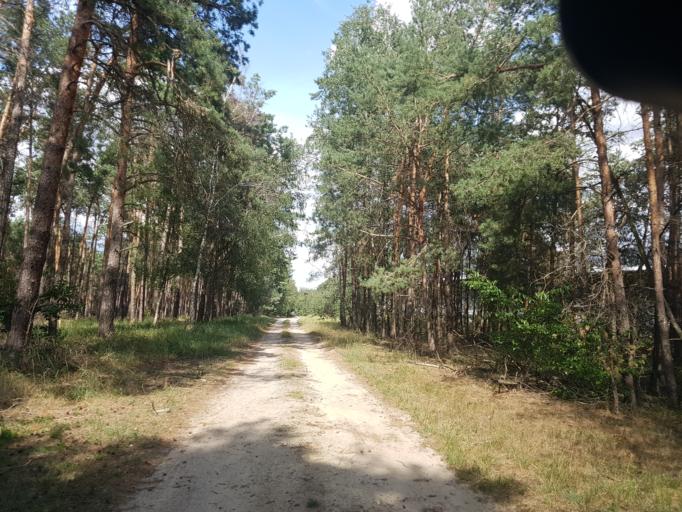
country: DE
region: Brandenburg
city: Schonborn
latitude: 51.6581
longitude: 13.4985
